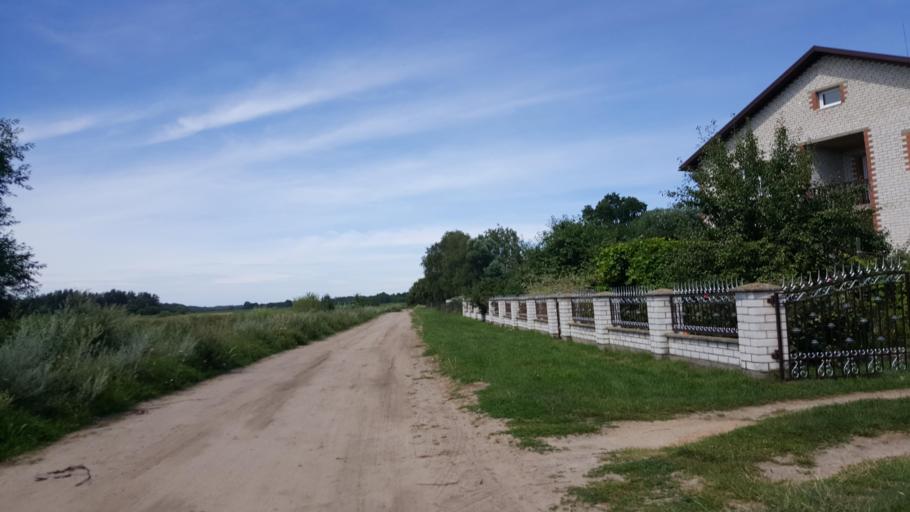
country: BY
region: Brest
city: Pruzhany
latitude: 52.5609
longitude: 24.2063
